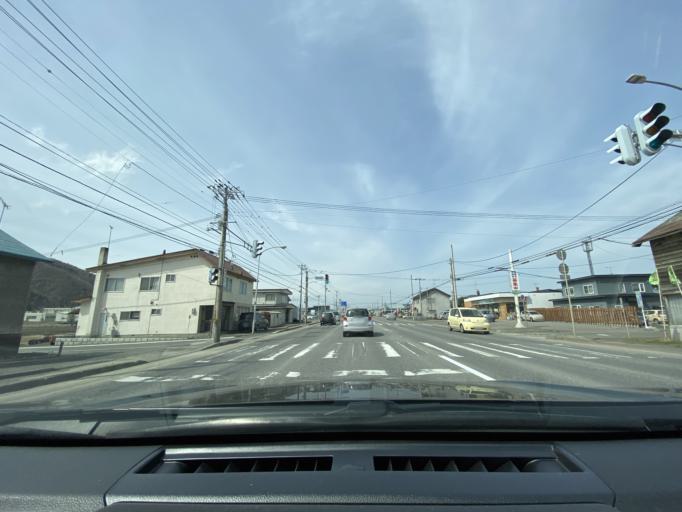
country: JP
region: Hokkaido
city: Kitami
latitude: 43.8033
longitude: 143.8108
